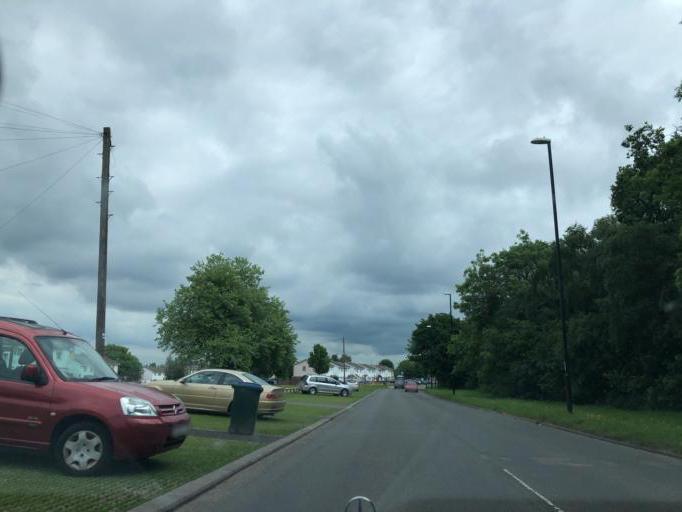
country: GB
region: England
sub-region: Warwickshire
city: Kenilworth
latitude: 52.3932
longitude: -1.5817
